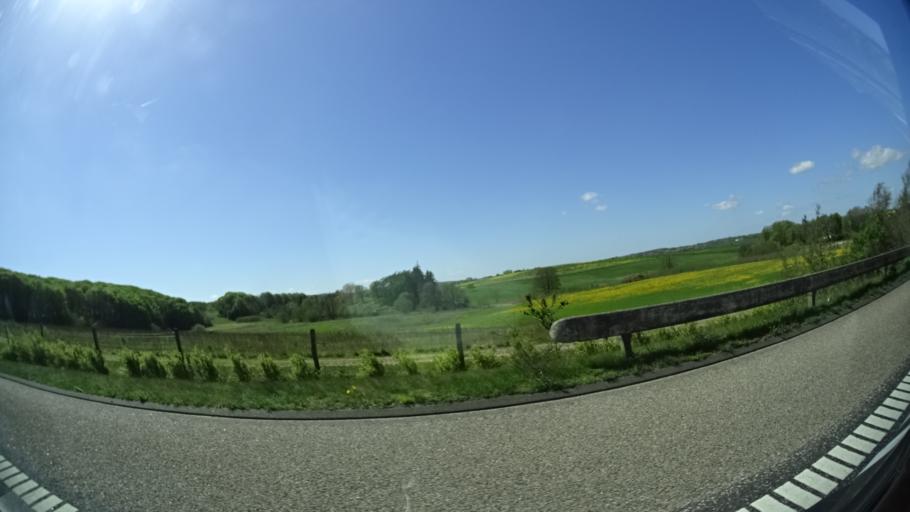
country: DK
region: Central Jutland
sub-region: Arhus Kommune
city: Framlev
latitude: 56.1277
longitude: 10.0344
